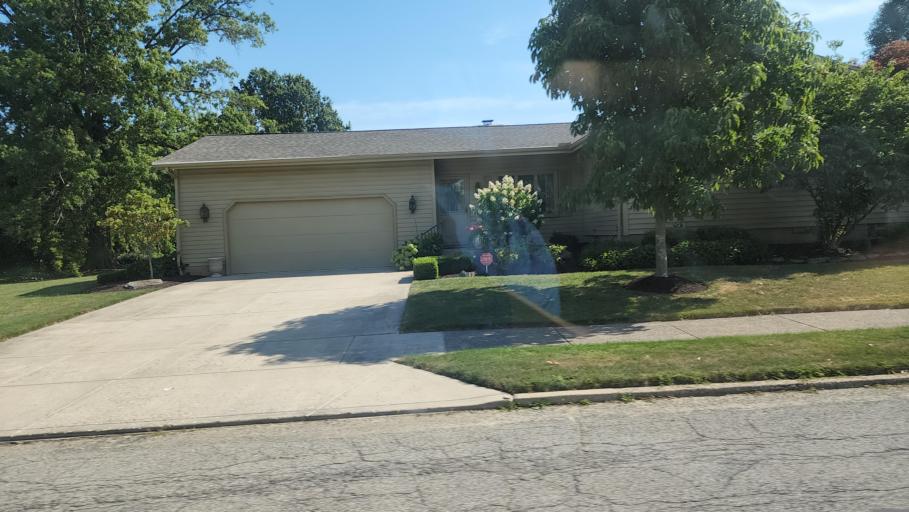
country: US
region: Ohio
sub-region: Trumbull County
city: Niles
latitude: 41.1931
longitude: -80.7535
